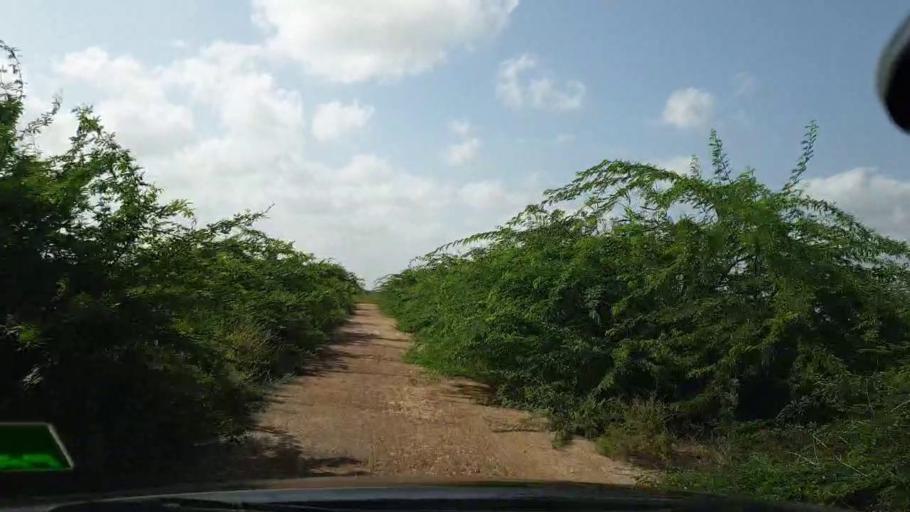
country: PK
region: Sindh
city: Kadhan
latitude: 24.6336
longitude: 69.1048
